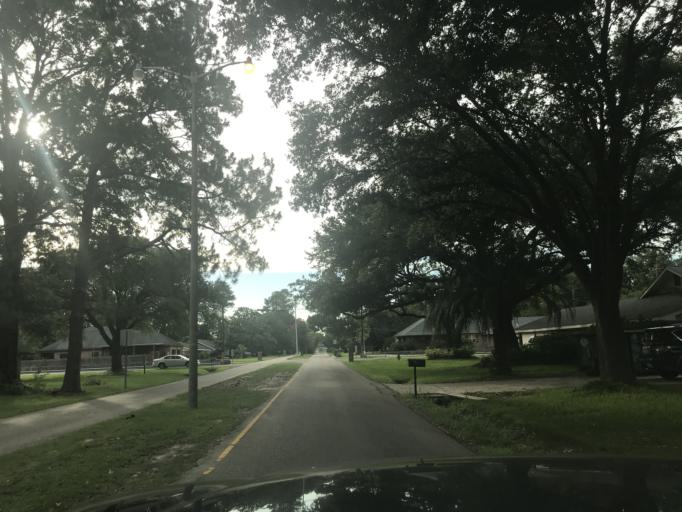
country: US
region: Louisiana
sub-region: Lafayette Parish
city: Lafayette
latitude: 30.1934
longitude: -92.0533
